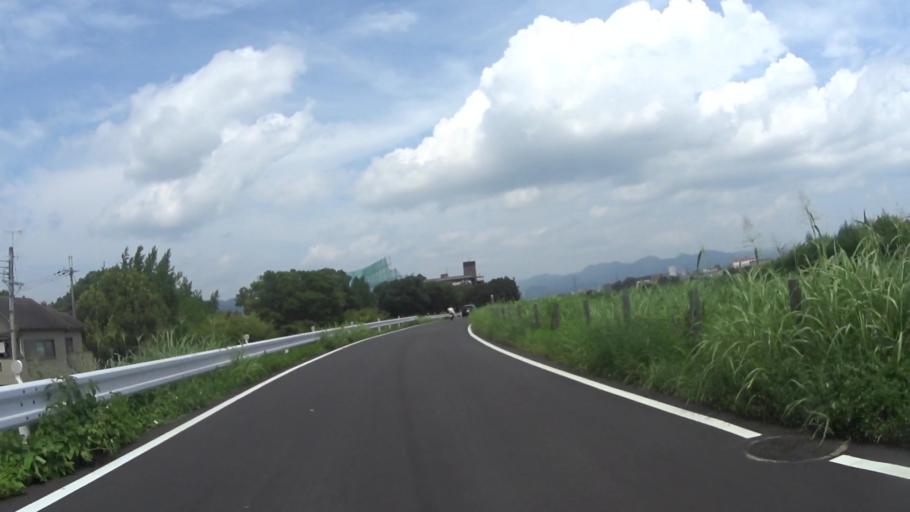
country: JP
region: Kyoto
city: Muko
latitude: 34.9754
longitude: 135.7175
